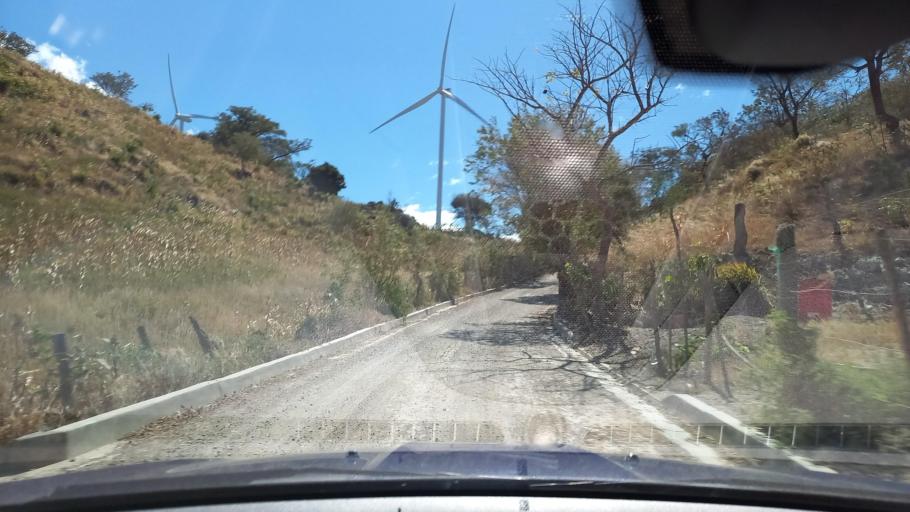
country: SV
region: Santa Ana
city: Metapan
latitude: 14.3728
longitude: -89.4881
